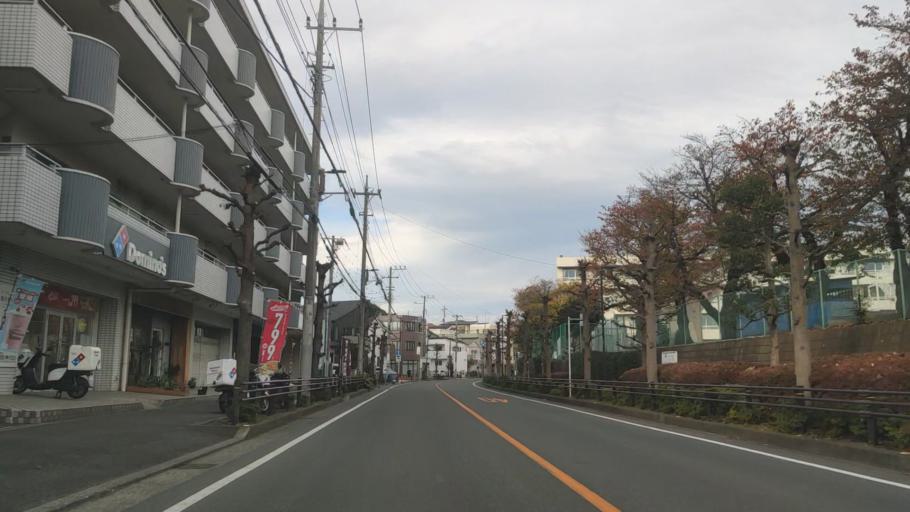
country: JP
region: Kanagawa
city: Atsugi
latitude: 35.4389
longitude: 139.4028
